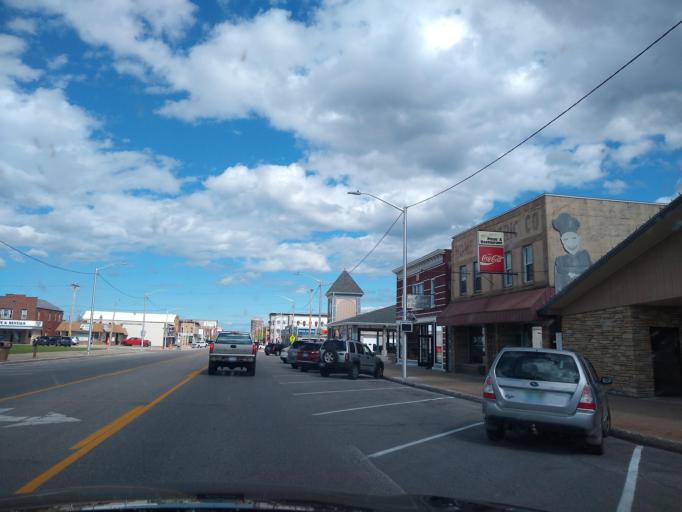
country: US
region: Michigan
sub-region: Delta County
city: Escanaba
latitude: 45.7457
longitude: -87.0699
